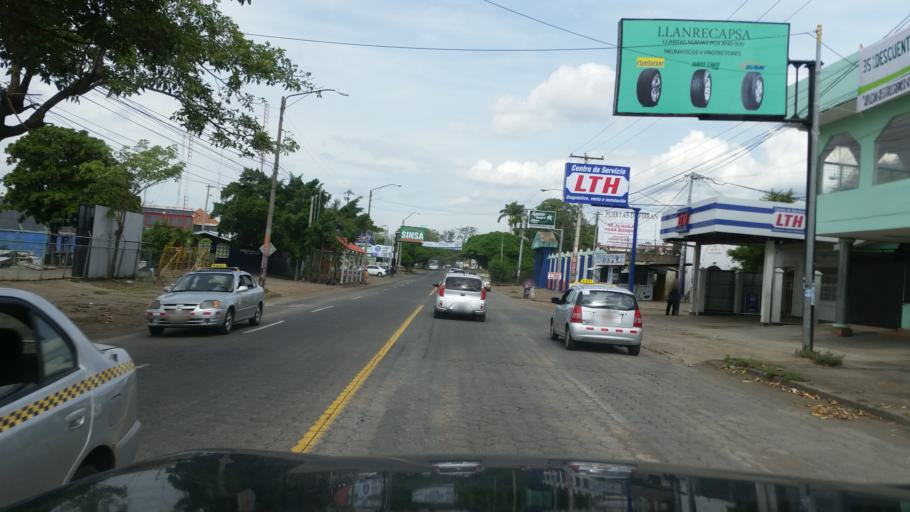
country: NI
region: Managua
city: Managua
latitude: 12.1364
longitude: -86.2868
